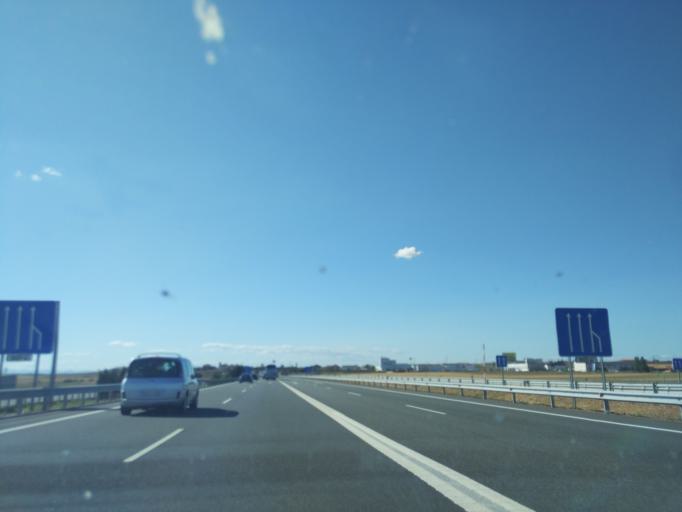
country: ES
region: Castille and Leon
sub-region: Provincia de Zamora
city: Castrogonzalo
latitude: 41.9733
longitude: -5.6029
